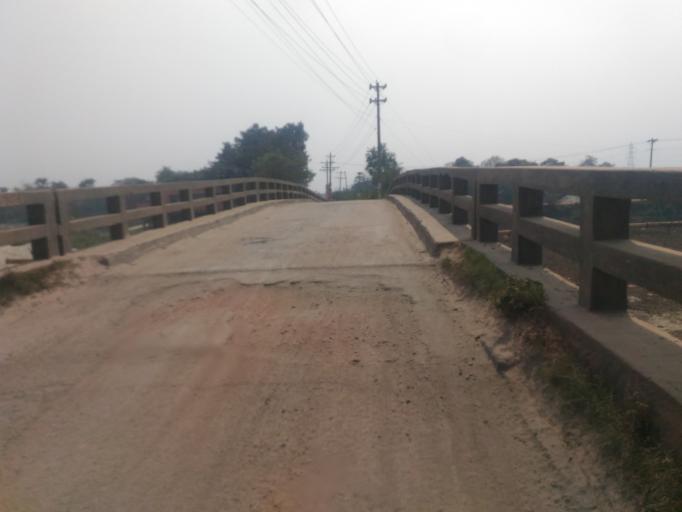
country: BD
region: Dhaka
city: Narayanganj
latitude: 23.6517
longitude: 90.4477
